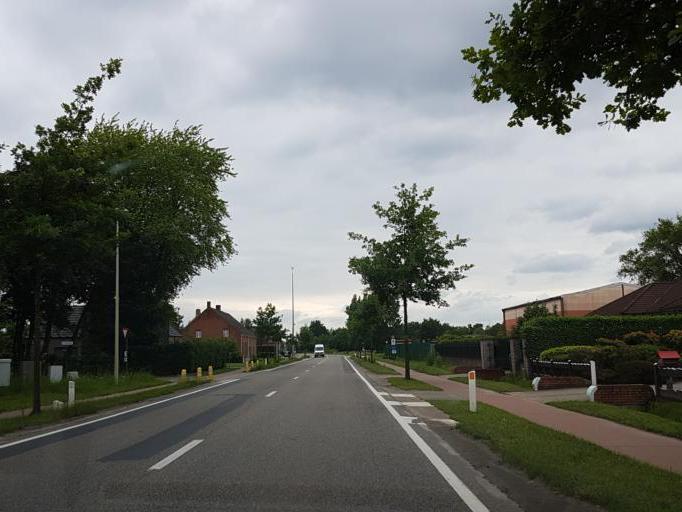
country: BE
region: Flanders
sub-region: Provincie Antwerpen
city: Oostmalle
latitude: 51.3244
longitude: 4.7419
